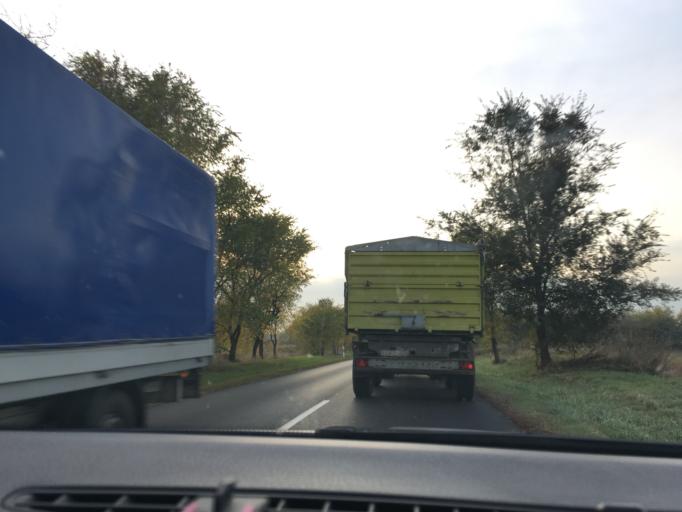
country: HU
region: Szabolcs-Szatmar-Bereg
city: Kallosemjen
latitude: 47.8586
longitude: 21.9451
